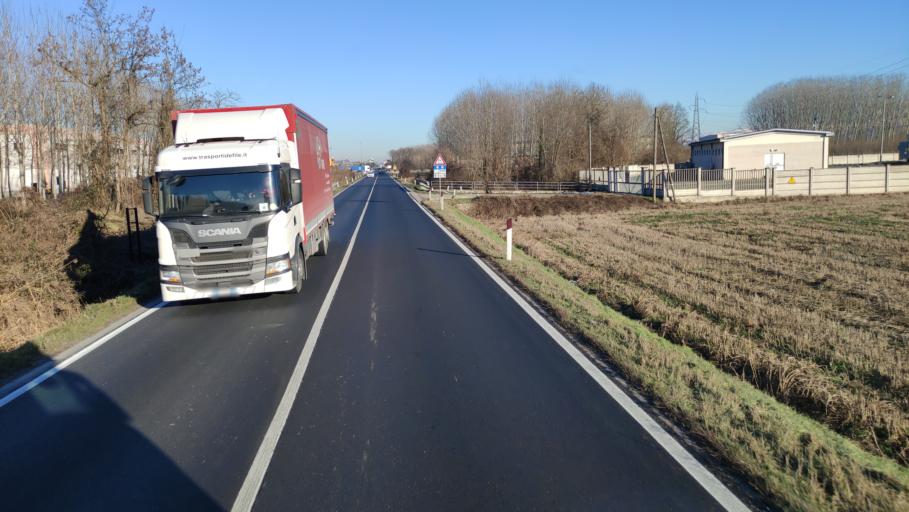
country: IT
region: Piedmont
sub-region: Provincia di Cuneo
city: Santa Vittoria d'Alba
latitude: 44.6966
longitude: 7.9515
